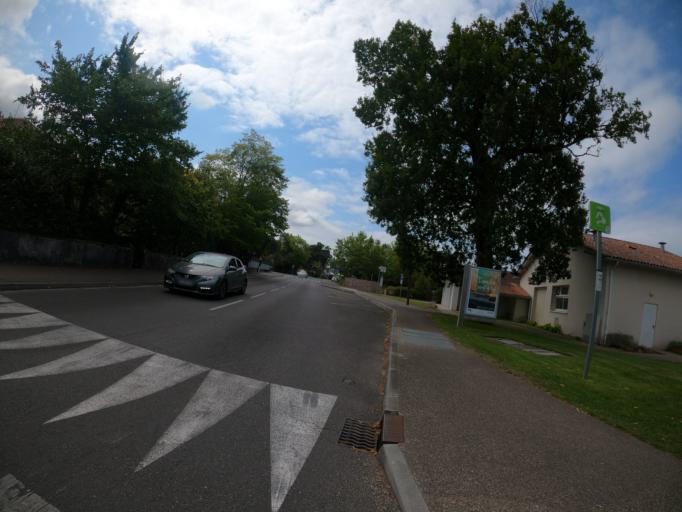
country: FR
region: Aquitaine
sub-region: Departement des Landes
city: Leon
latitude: 43.8486
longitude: -1.3581
